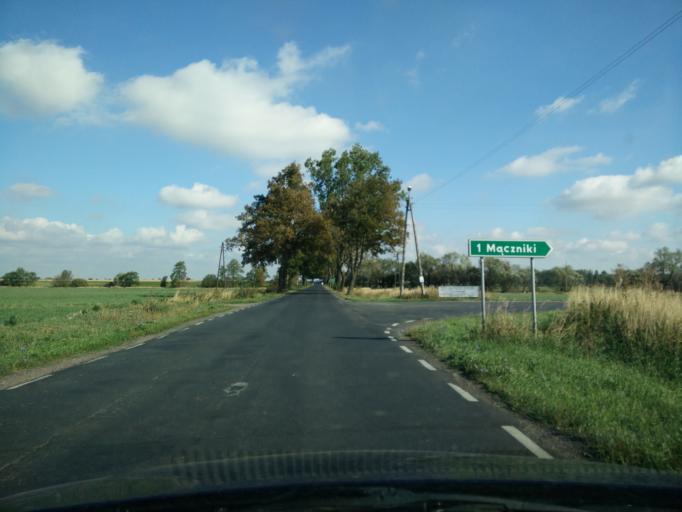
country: PL
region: Greater Poland Voivodeship
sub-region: Powiat sredzki
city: Sroda Wielkopolska
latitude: 52.2556
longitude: 17.3002
